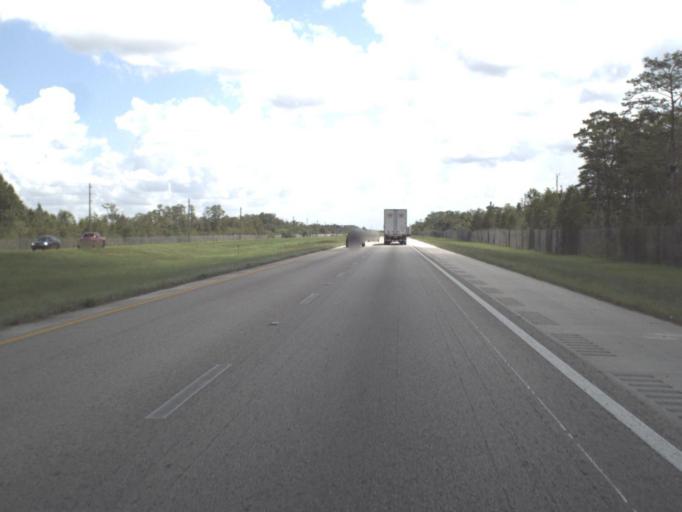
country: US
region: Florida
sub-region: Collier County
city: Immokalee
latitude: 26.1550
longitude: -81.3057
